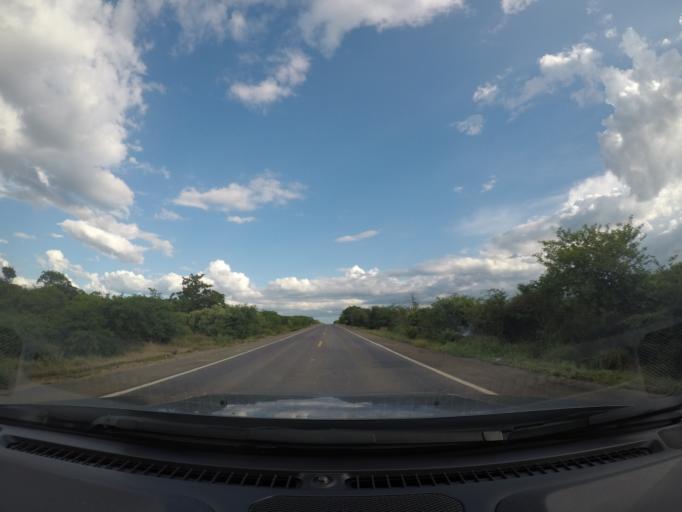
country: BR
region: Bahia
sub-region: Oliveira Dos Brejinhos
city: Beira Rio
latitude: -12.1874
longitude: -42.8271
